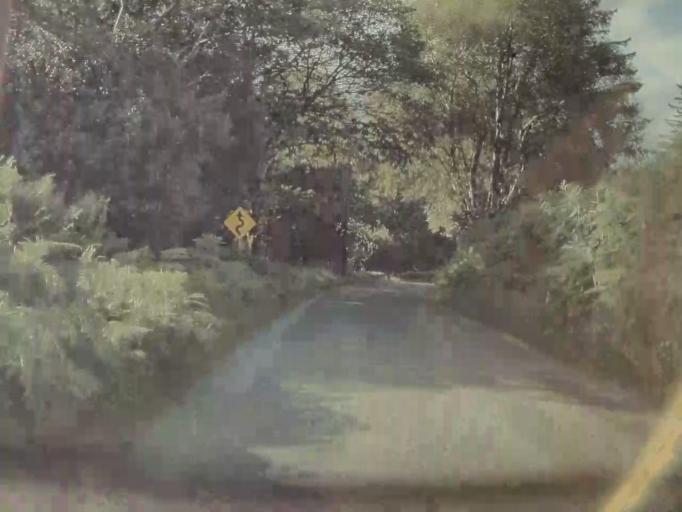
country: IE
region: Leinster
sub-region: Wicklow
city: Rathdrum
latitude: 53.0397
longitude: -6.3249
